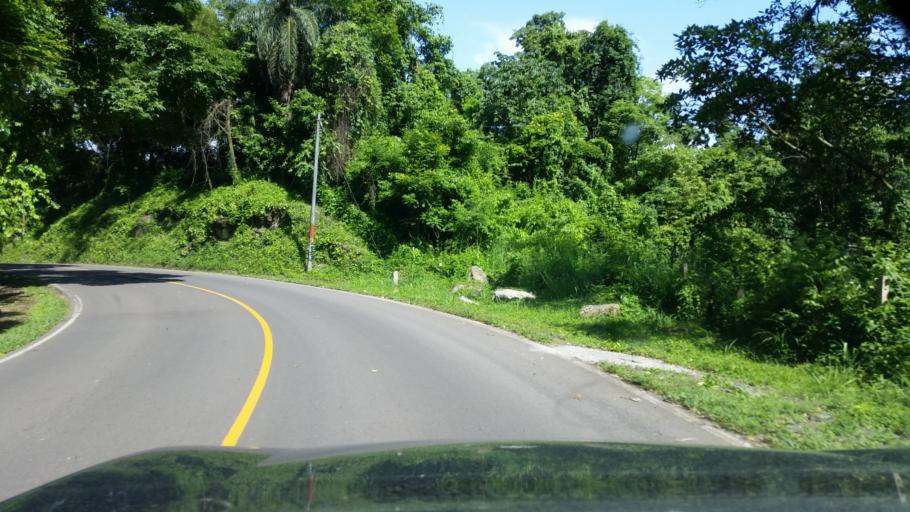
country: NI
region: Matagalpa
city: San Ramon
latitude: 13.0224
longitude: -85.7902
